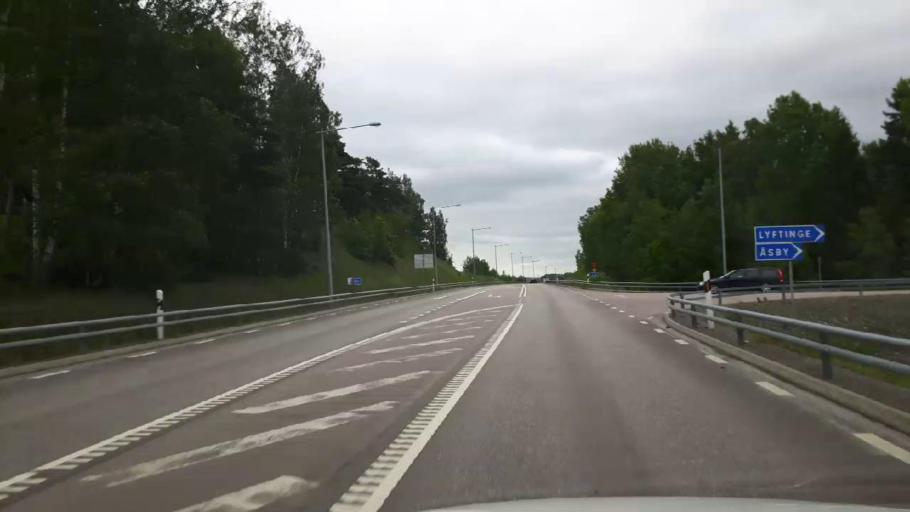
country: SE
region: Vaestmanland
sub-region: Kopings Kommun
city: Kolsva
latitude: 59.5513
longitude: 15.9094
